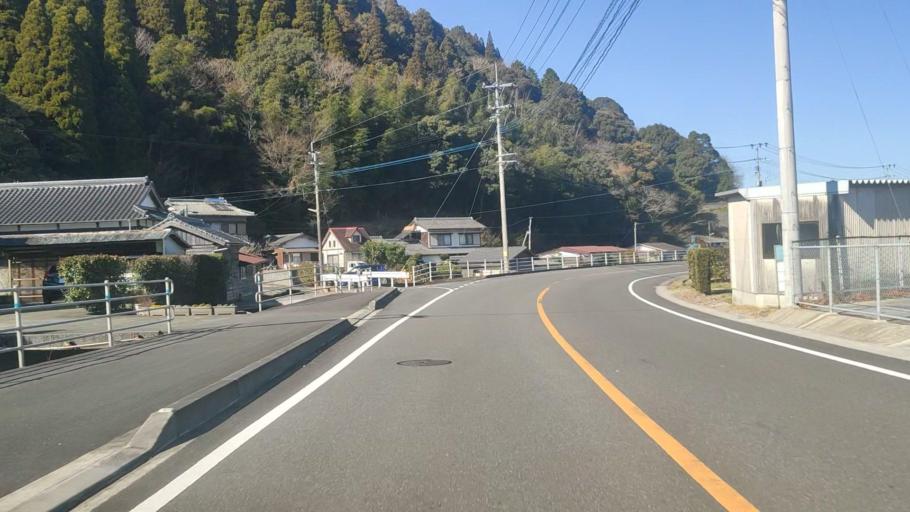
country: JP
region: Oita
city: Saiki
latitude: 32.9280
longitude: 131.9221
